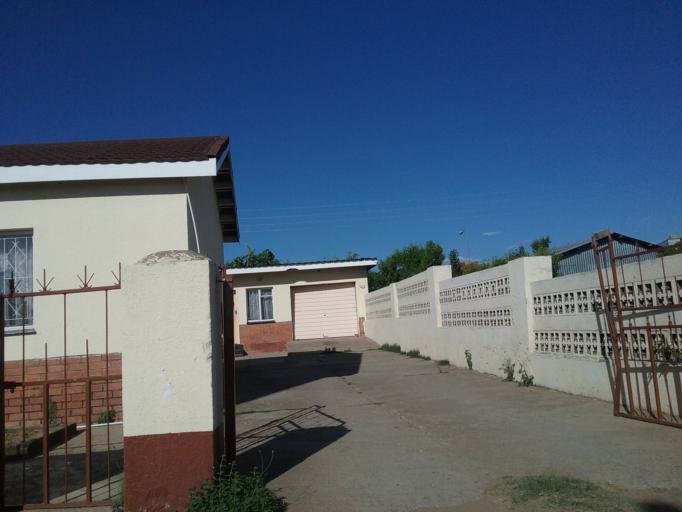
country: LS
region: Maseru
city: Maseru
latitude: -29.3131
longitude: 27.5004
